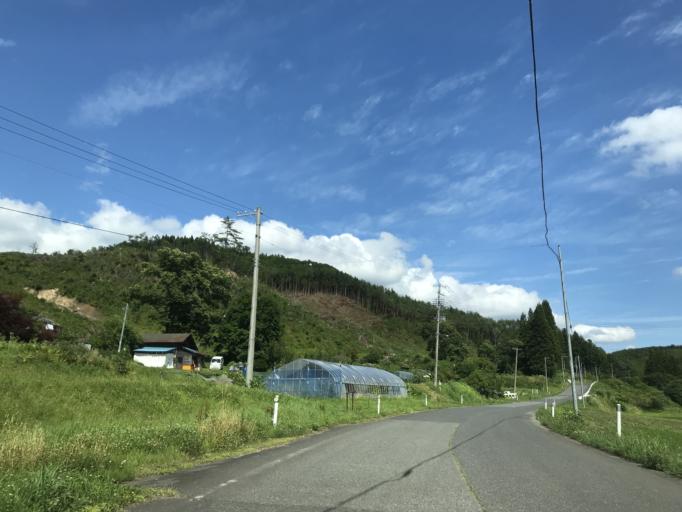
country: JP
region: Iwate
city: Ichinoseki
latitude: 38.9637
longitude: 140.9530
